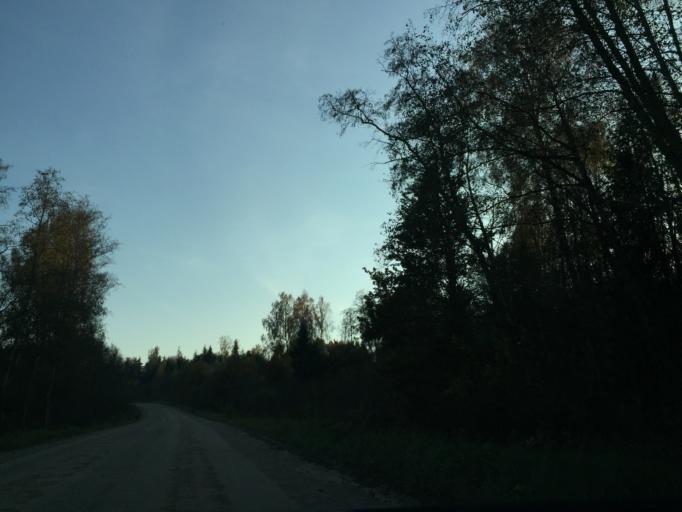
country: LV
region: Vainode
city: Vainode
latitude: 56.5764
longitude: 21.8451
